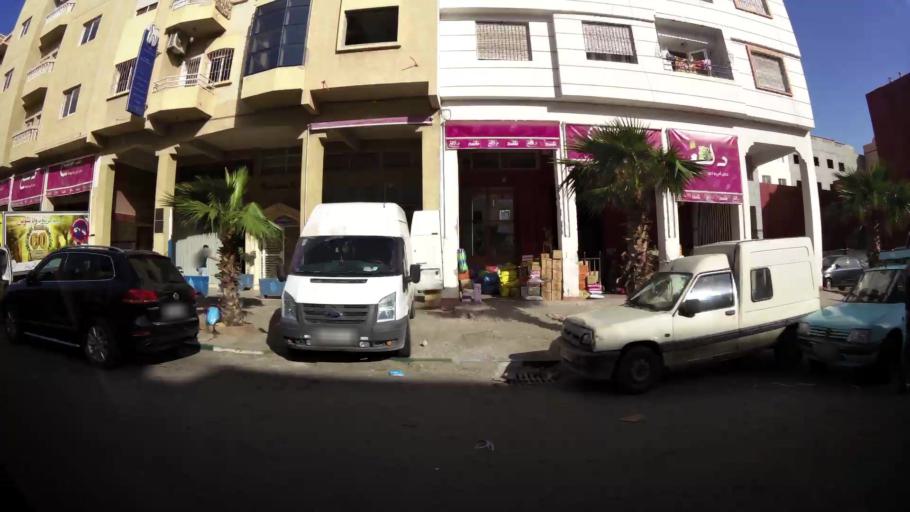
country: MA
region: Souss-Massa-Draa
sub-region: Inezgane-Ait Mellou
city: Inezgane
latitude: 30.3624
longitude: -9.5262
